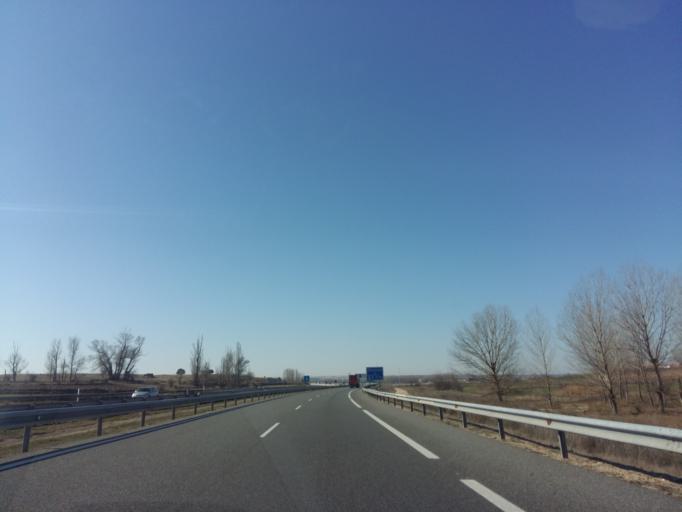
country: ES
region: Castille and Leon
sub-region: Provincia de Burgos
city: Villalba de Duero
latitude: 41.6853
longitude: -3.7191
